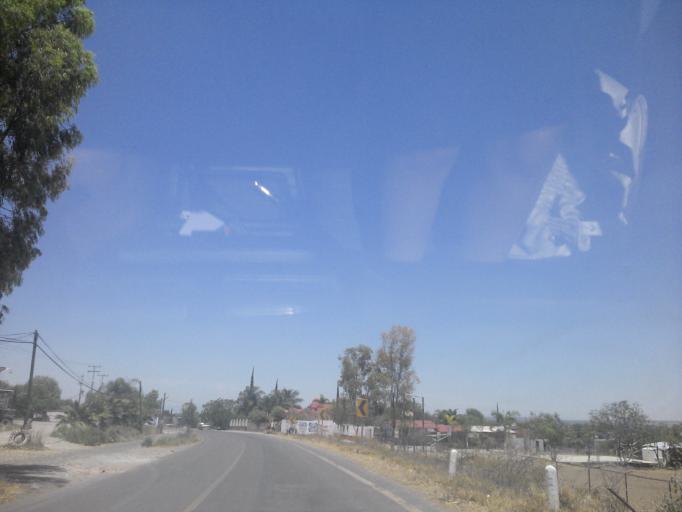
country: MX
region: Guanajuato
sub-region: San Francisco del Rincon
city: San Ignacio de Hidalgo
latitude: 20.8983
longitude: -101.9205
